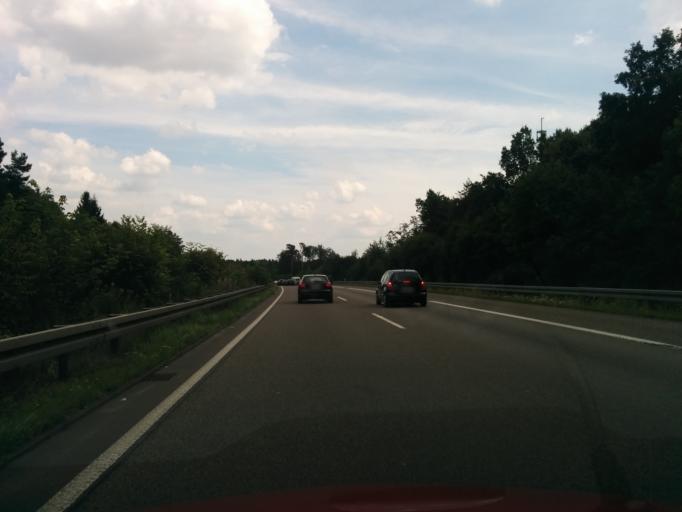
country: DE
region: Hesse
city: Romrod
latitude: 50.7118
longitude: 9.1514
